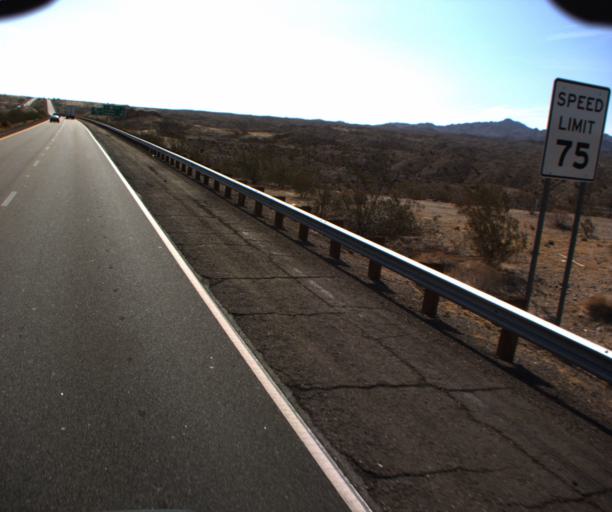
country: US
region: Arizona
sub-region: Mohave County
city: Desert Hills
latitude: 34.7184
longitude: -114.4664
